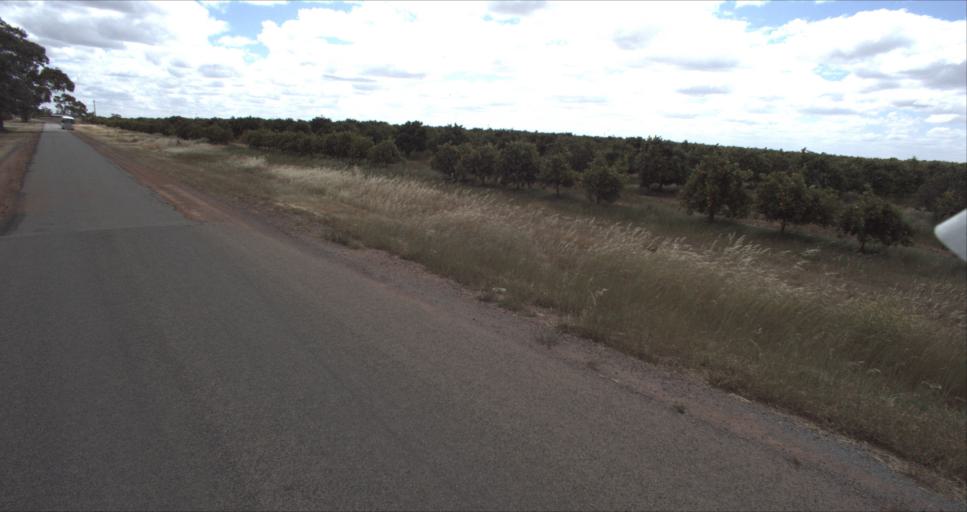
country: AU
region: New South Wales
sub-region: Leeton
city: Leeton
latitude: -34.5891
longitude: 146.3900
